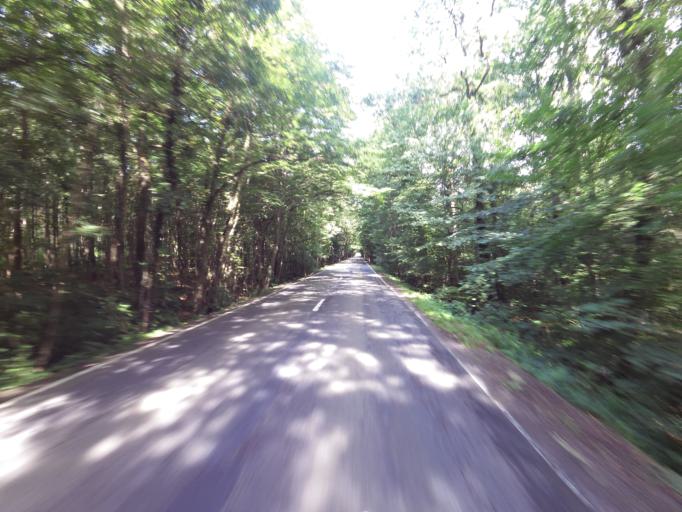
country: BE
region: Wallonia
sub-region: Province du Luxembourg
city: Hotton
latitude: 50.2752
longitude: 5.4798
